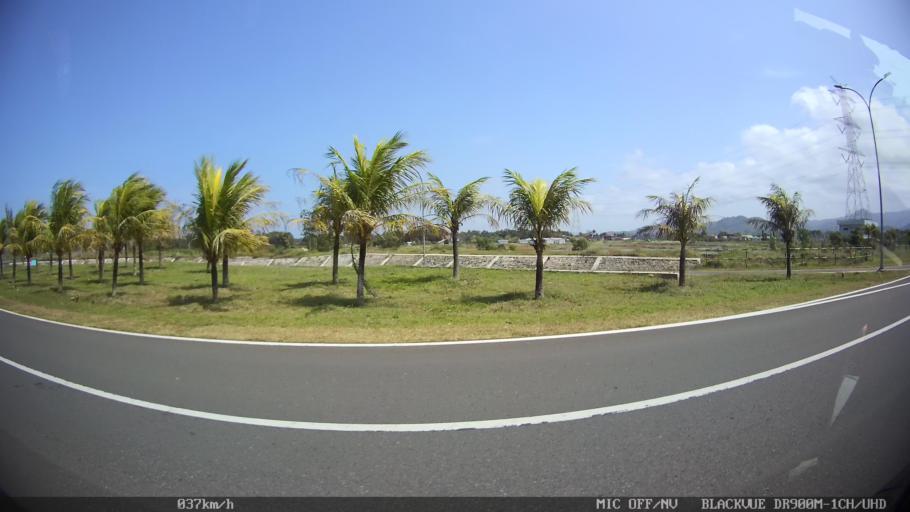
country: ID
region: Daerah Istimewa Yogyakarta
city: Srandakan
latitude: -7.8912
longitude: 110.0616
